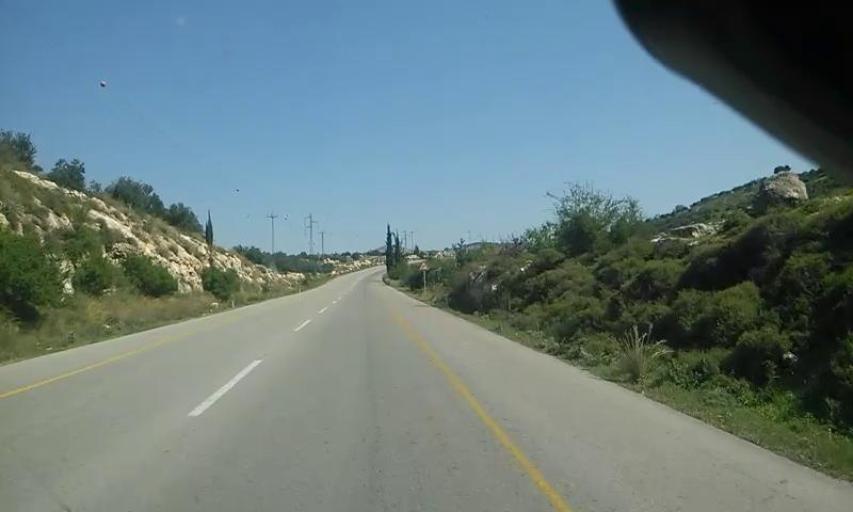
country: PS
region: West Bank
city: Tarqumya
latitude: 31.5628
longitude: 34.9994
